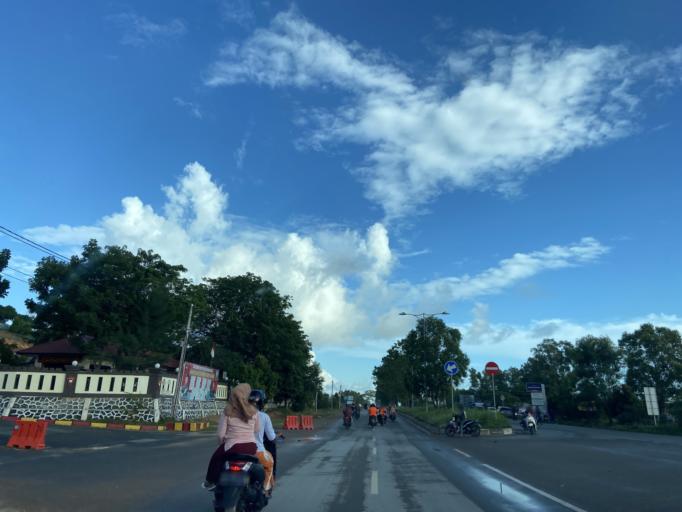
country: SG
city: Singapore
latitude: 1.0308
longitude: 104.0031
